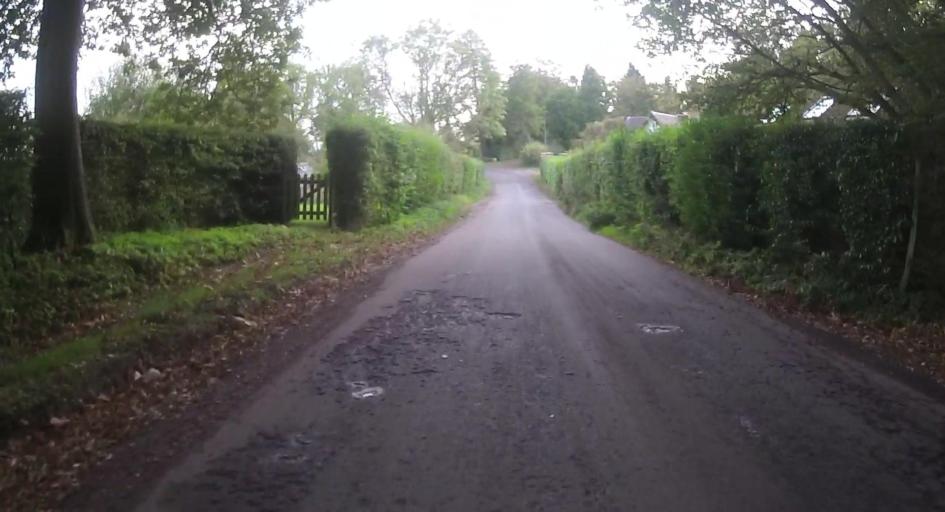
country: GB
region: England
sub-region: West Berkshire
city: Thatcham
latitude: 51.4043
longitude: -1.1864
